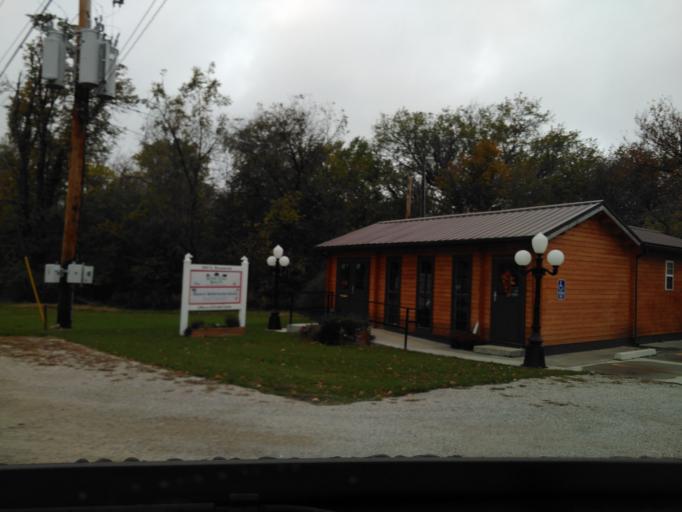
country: US
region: Illinois
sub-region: Bond County
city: Greenville
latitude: 38.9014
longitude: -89.4012
